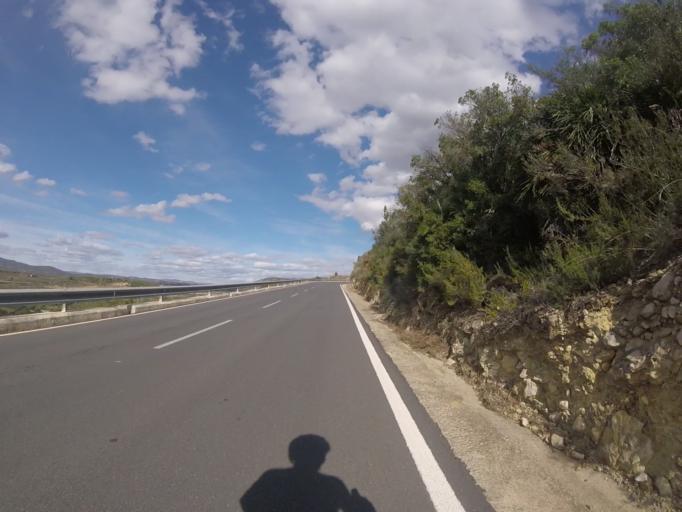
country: ES
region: Valencia
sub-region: Provincia de Castello
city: Cuevas de Vinroma
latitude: 40.3165
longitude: 0.1293
